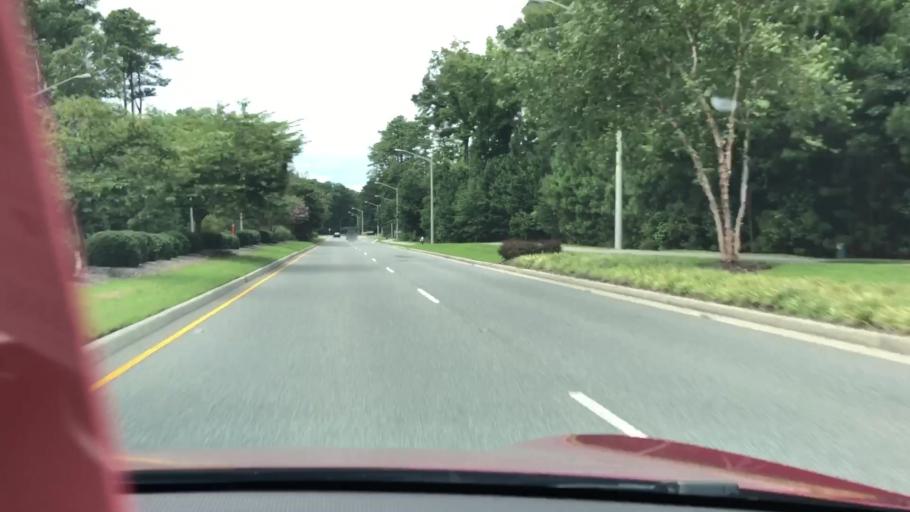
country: US
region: Virginia
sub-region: City of Virginia Beach
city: Virginia Beach
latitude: 36.8137
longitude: -75.9958
